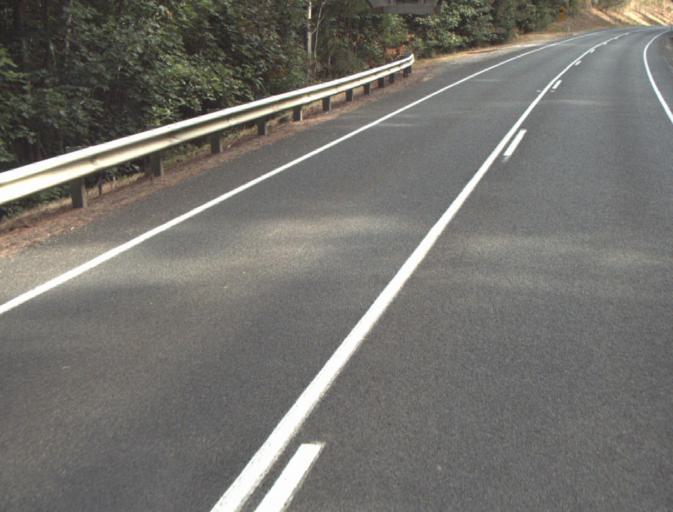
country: AU
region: Tasmania
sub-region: Launceston
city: Mayfield
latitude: -41.3032
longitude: 147.2052
